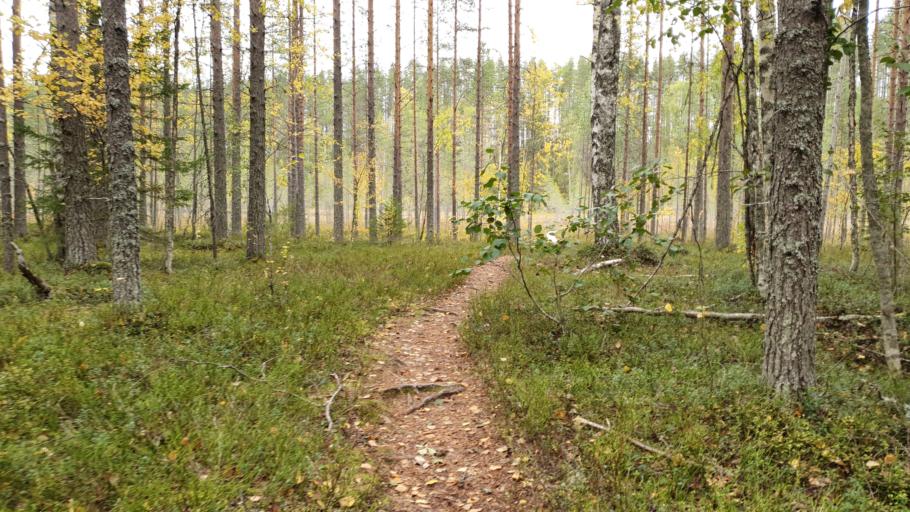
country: FI
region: Kainuu
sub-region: Kehys-Kainuu
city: Kuhmo
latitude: 64.2914
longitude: 29.3980
